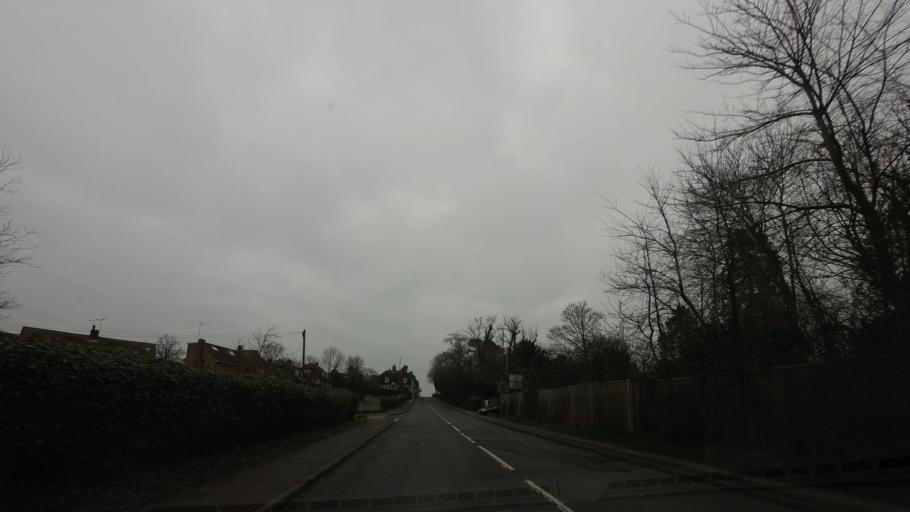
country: GB
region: England
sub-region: Kent
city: Staplehurst
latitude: 51.1567
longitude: 0.5524
